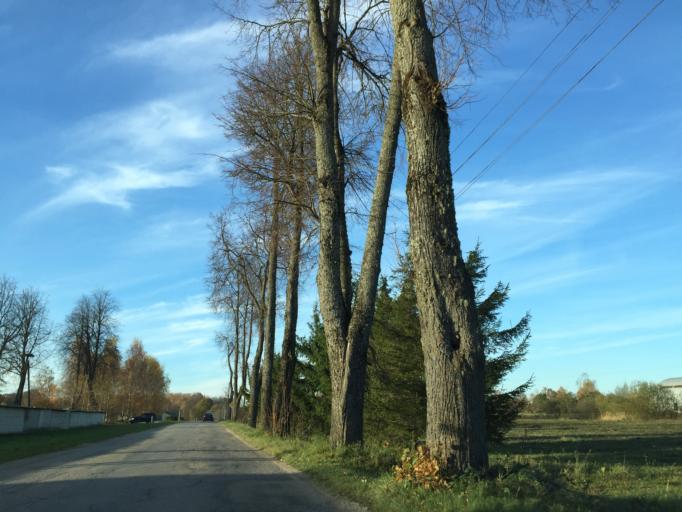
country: LV
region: Skriveri
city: Skriveri
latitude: 56.6297
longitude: 25.1221
